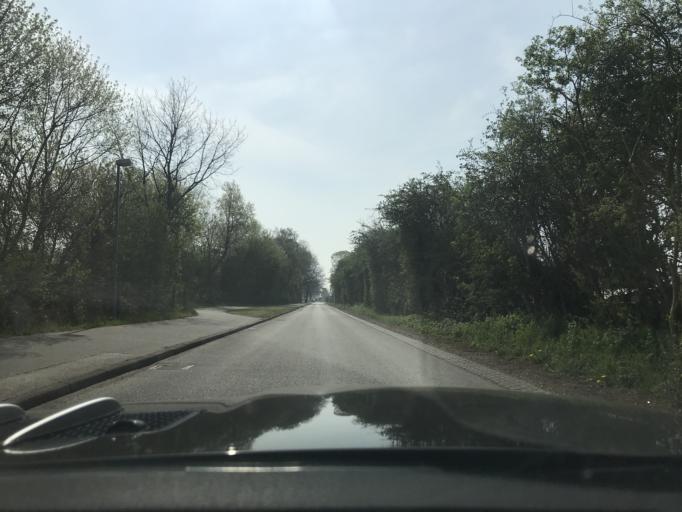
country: DE
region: Schleswig-Holstein
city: Gromitz
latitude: 54.1610
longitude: 10.9864
